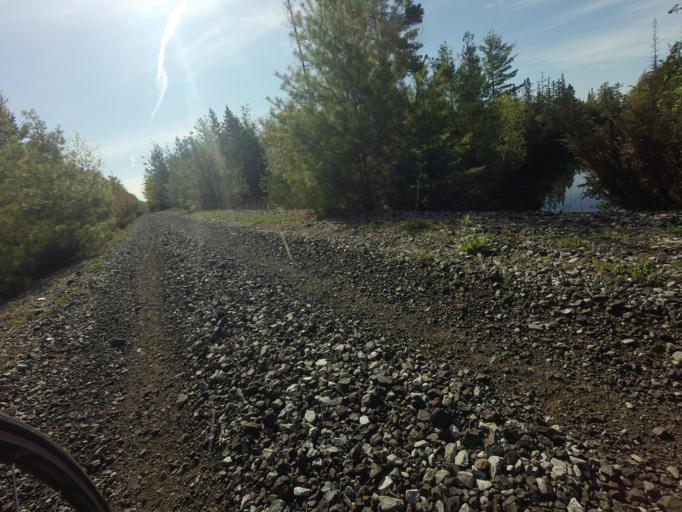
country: CA
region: Ontario
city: Arnprior
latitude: 45.4710
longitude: -76.2991
